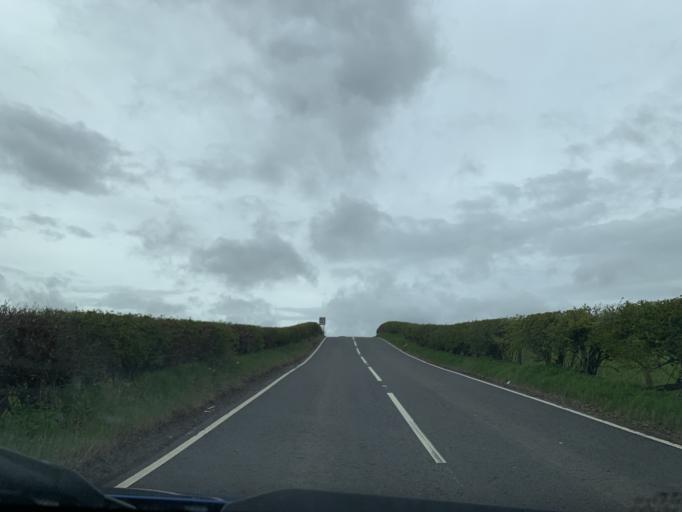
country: GB
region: Scotland
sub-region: East Renfrewshire
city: Barrhead
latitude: 55.7656
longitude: -4.3749
